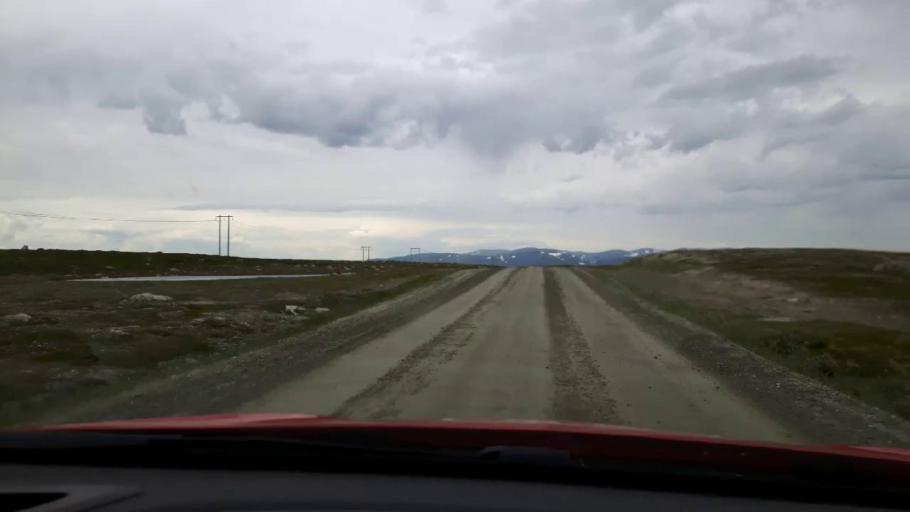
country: SE
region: Jaemtland
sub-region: Are Kommun
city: Are
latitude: 62.7499
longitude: 12.7486
